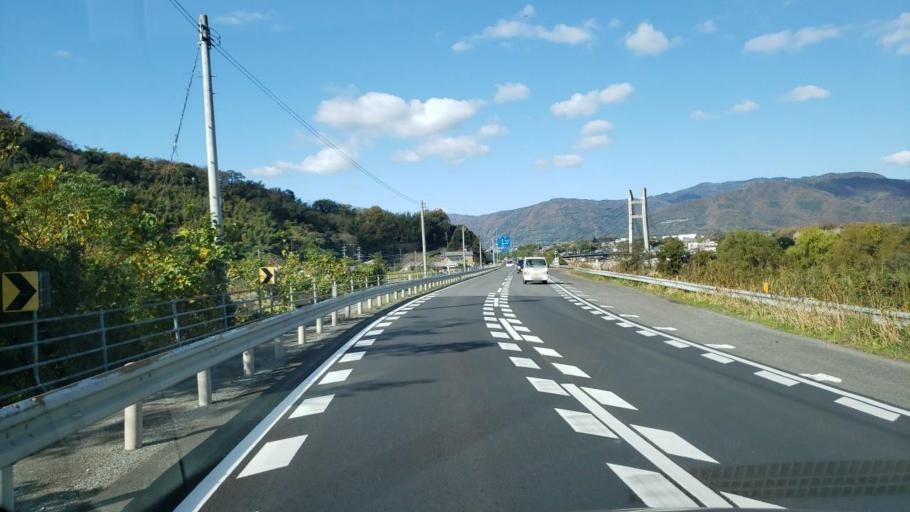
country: JP
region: Tokushima
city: Wakimachi
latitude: 34.0624
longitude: 134.1994
